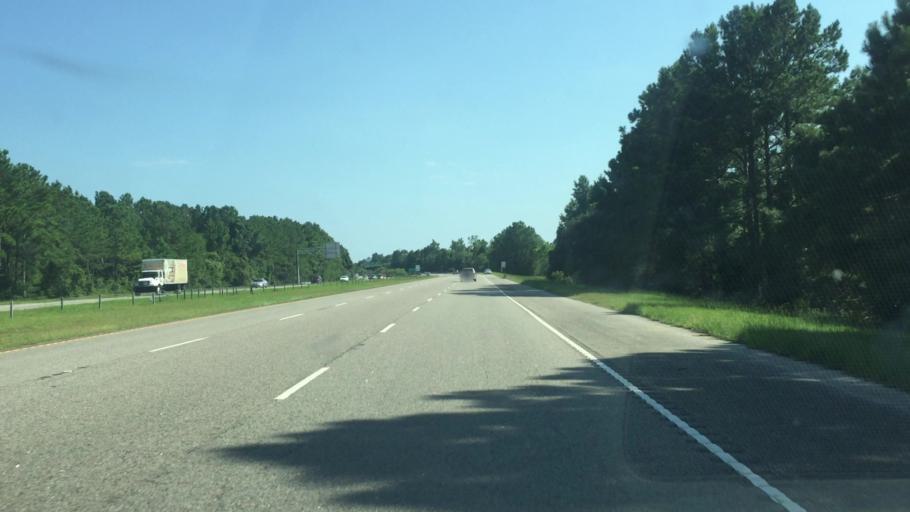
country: US
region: South Carolina
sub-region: Horry County
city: North Myrtle Beach
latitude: 33.8019
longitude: -78.7793
